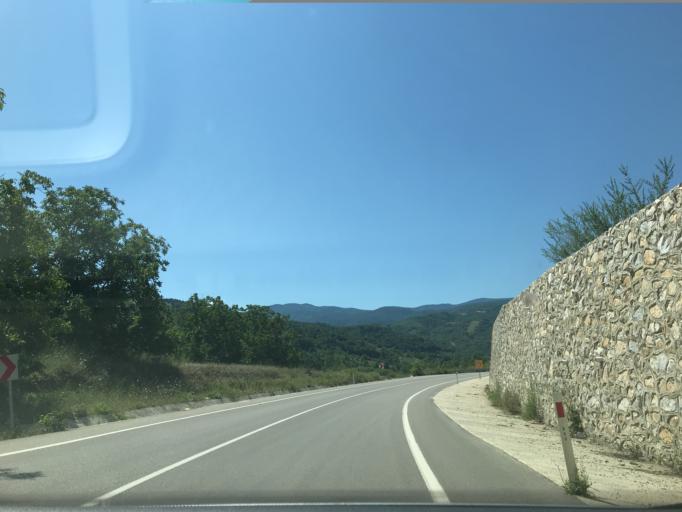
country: TR
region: Bursa
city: Tahtakopru
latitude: 39.9734
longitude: 29.6053
